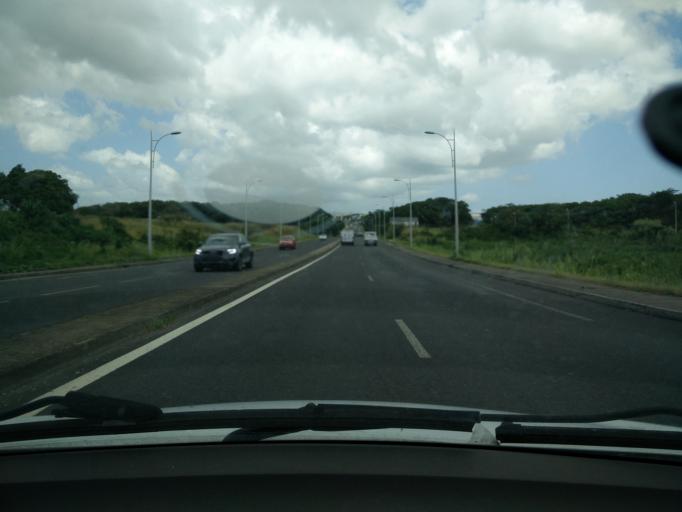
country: GP
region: Guadeloupe
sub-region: Guadeloupe
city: Baie-Mahault
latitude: 16.2394
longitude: -61.5755
